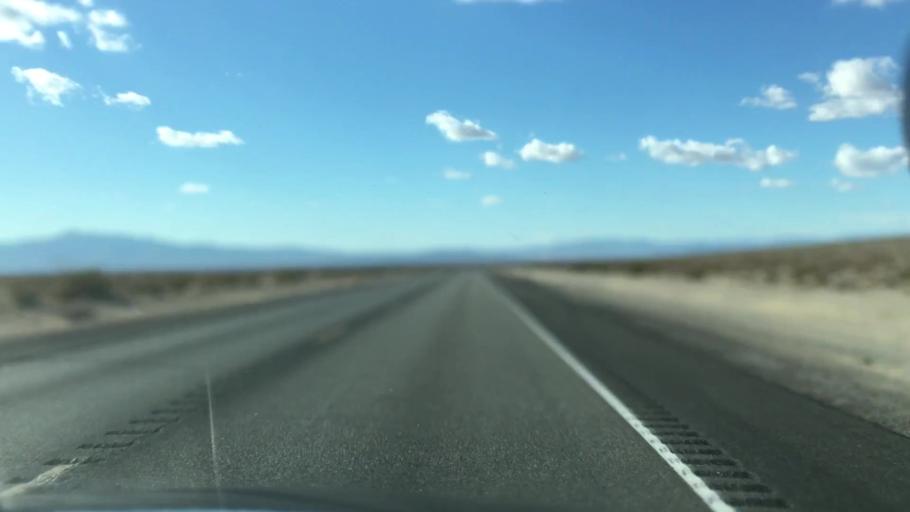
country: US
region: Nevada
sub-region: Nye County
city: Beatty
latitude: 36.6318
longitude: -116.3365
